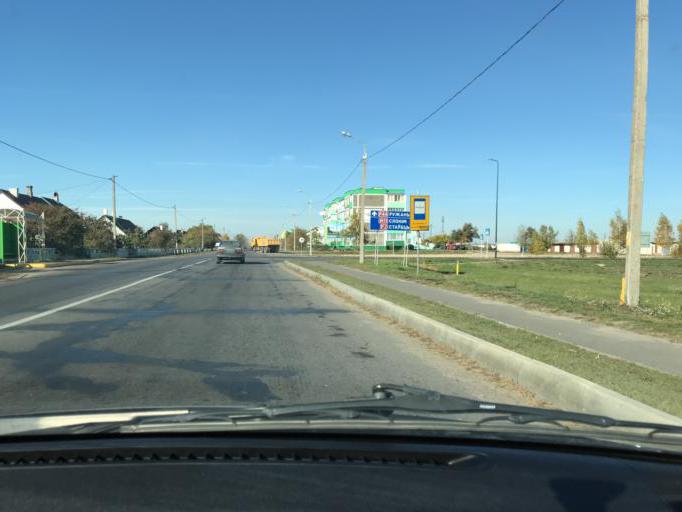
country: BY
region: Brest
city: Ivatsevichy
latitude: 52.7036
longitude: 25.3601
